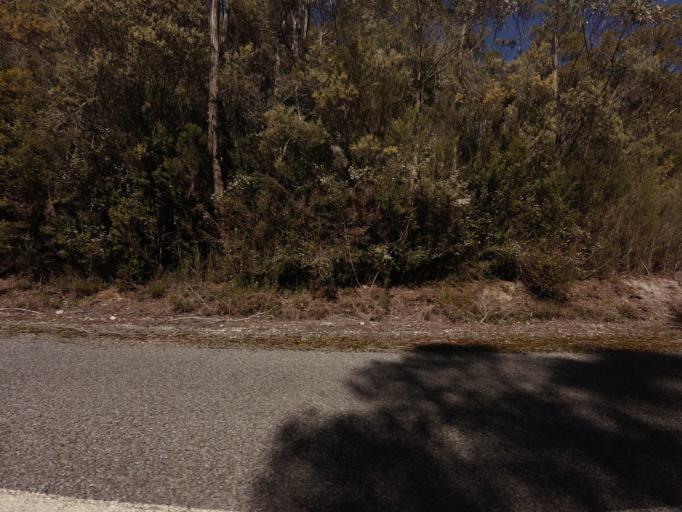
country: AU
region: Tasmania
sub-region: Derwent Valley
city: New Norfolk
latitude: -42.7557
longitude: 146.4096
